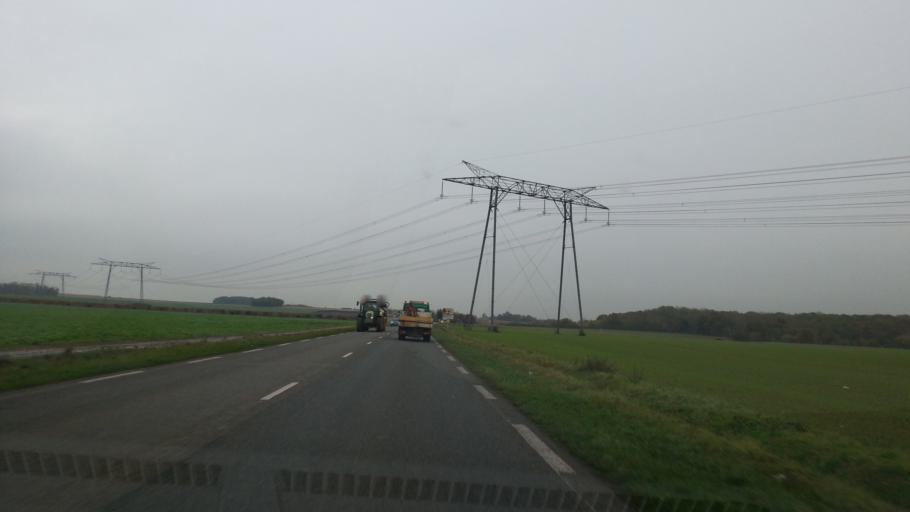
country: FR
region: Picardie
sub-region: Departement de l'Oise
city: Boran-sur-Oise
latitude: 49.1720
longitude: 2.3476
